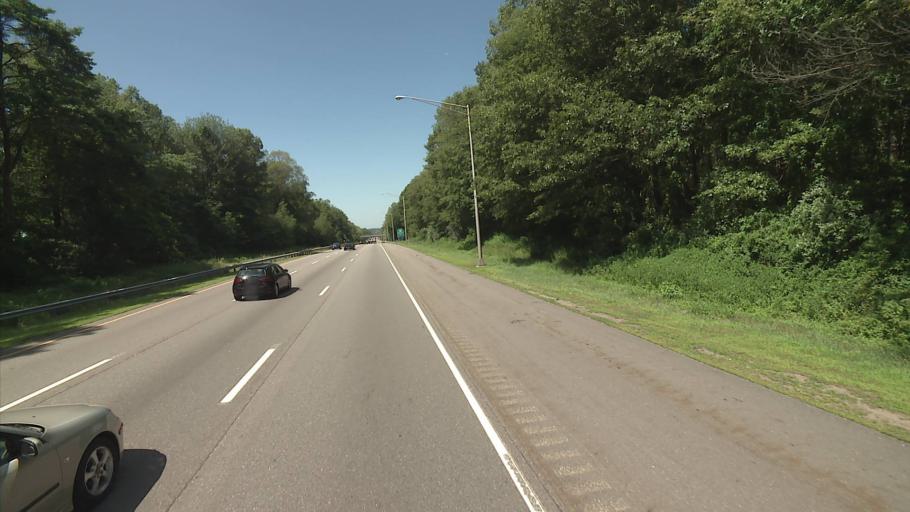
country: US
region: Connecticut
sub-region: New London County
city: Poquonock Bridge
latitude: 41.3702
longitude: -72.0016
